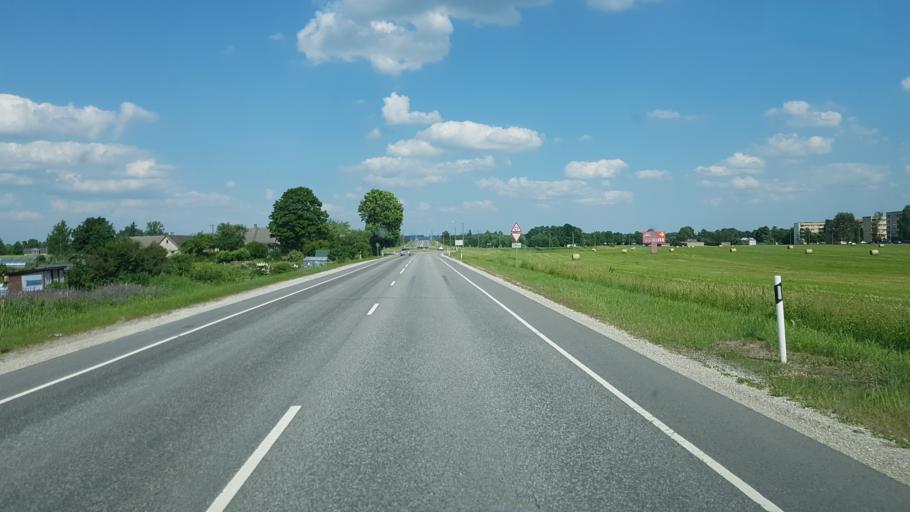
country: EE
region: Jogevamaa
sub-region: Jogeva linn
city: Jogeva
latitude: 58.7502
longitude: 26.3839
